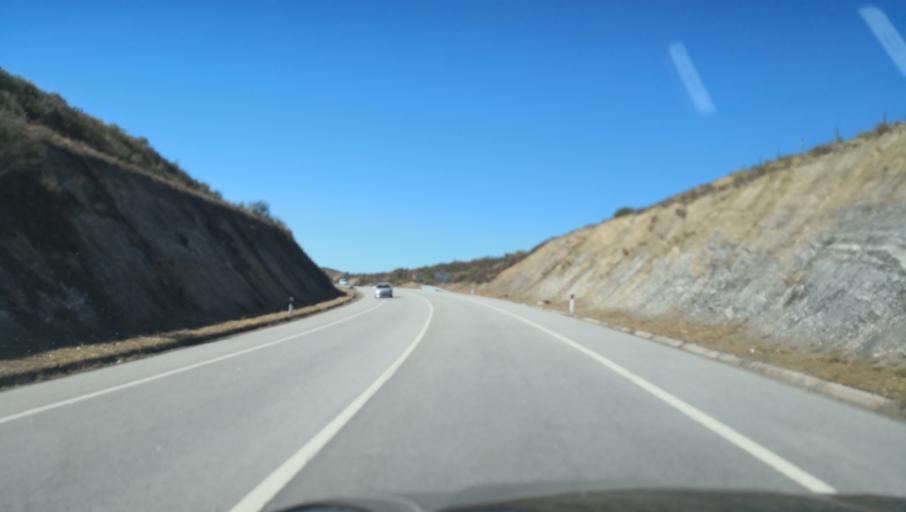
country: PT
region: Braganca
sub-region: Mirandela
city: Mirandela
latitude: 41.5180
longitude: -7.2299
